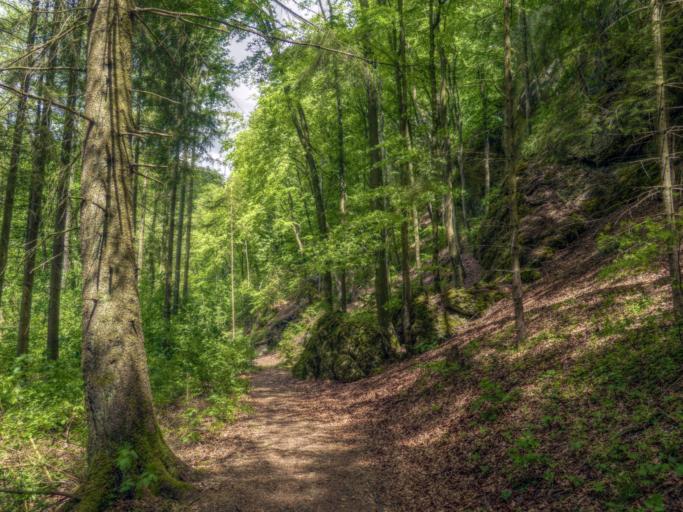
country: DE
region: Bavaria
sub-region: Upper Franconia
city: Stadelhofen
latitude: 50.0305
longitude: 11.2024
